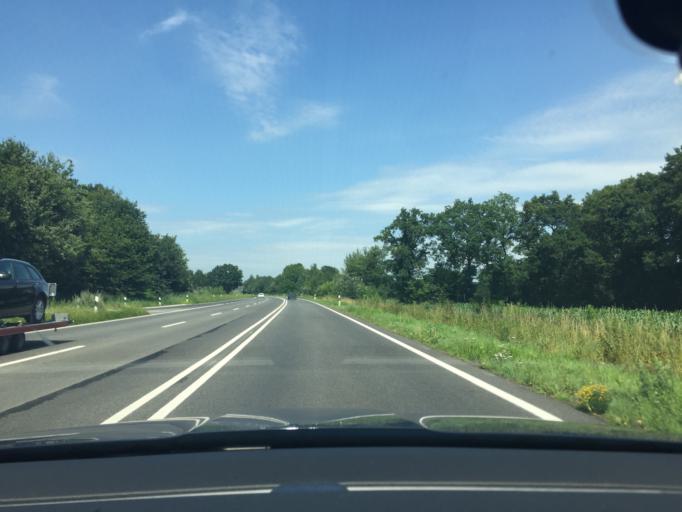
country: DE
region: Lower Saxony
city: Filsum
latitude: 53.2401
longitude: 7.6404
